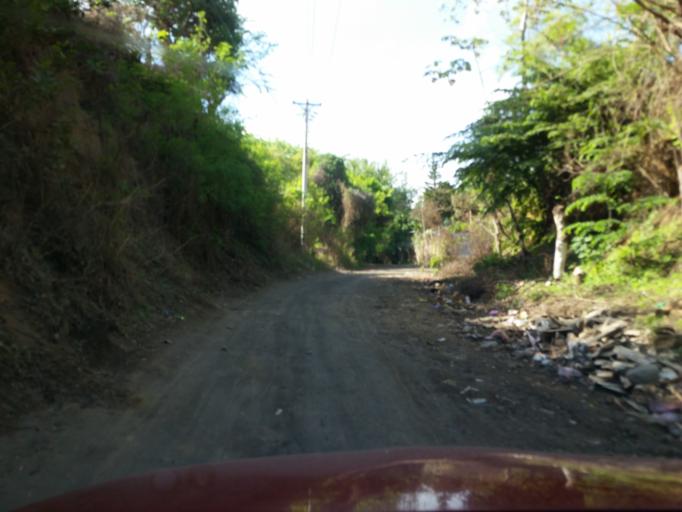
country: NI
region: Managua
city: Managua
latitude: 12.0805
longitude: -86.2588
